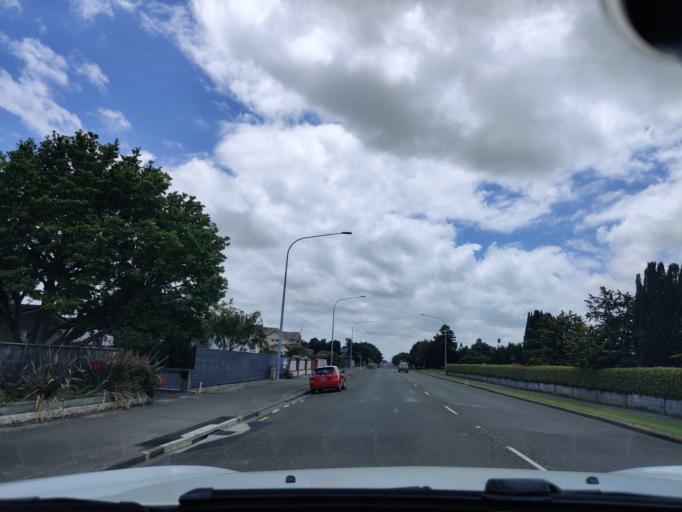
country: NZ
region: Manawatu-Wanganui
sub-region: Palmerston North City
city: Palmerston North
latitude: -40.3592
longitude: 175.6309
